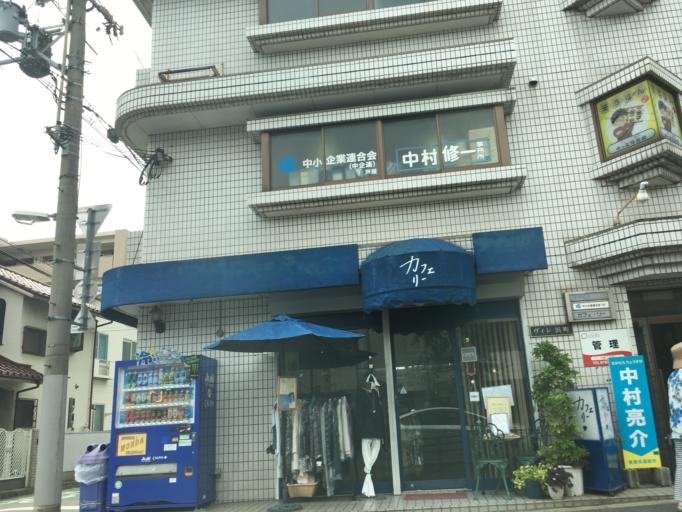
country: JP
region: Hyogo
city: Ashiya
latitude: 34.7300
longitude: 135.3172
